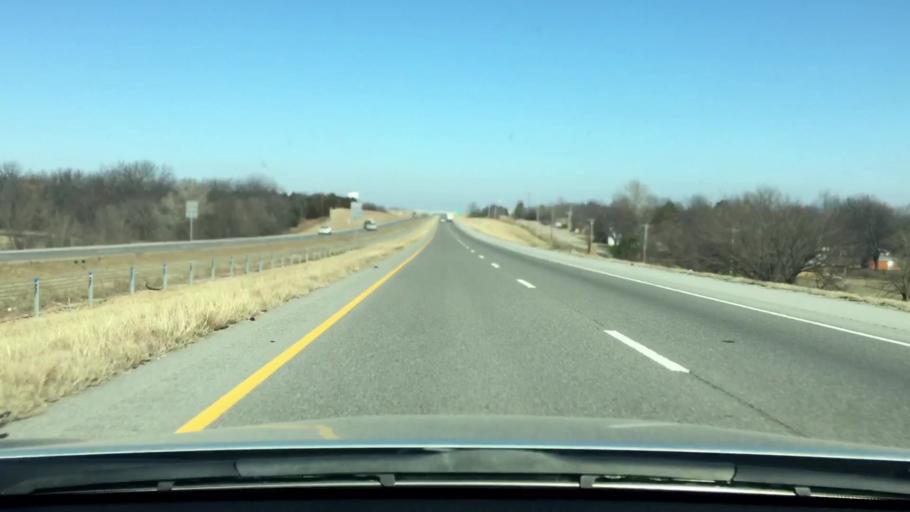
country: US
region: Oklahoma
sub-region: McClain County
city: Purcell
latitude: 34.9693
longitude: -97.3705
